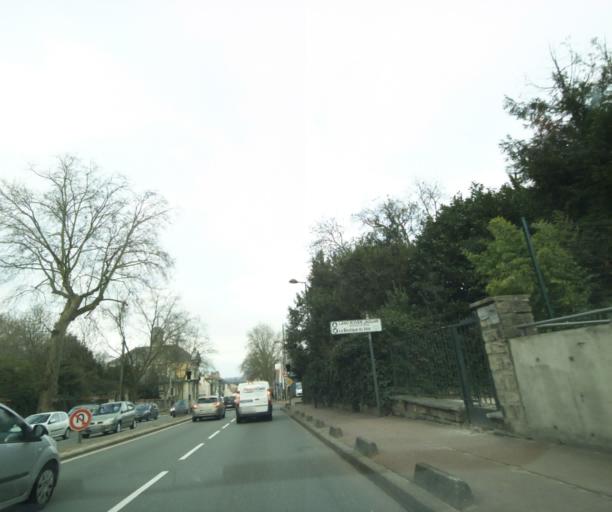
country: FR
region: Ile-de-France
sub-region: Departement des Yvelines
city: Le Port-Marly
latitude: 48.8771
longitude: 2.1060
